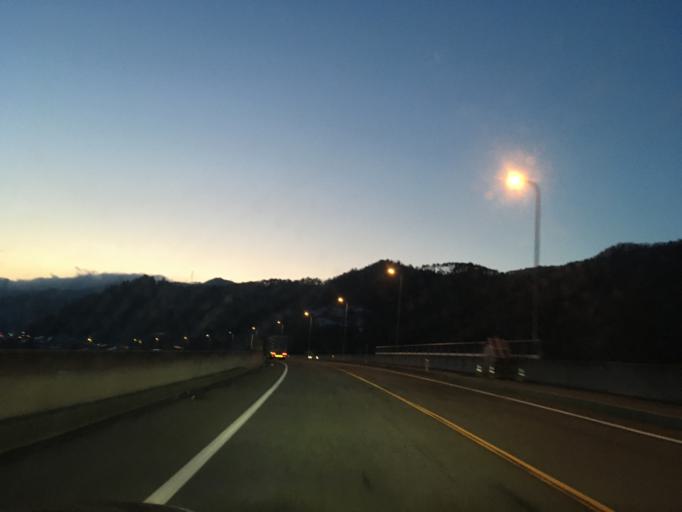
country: JP
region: Yamagata
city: Kaminoyama
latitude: 38.1296
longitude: 140.2493
